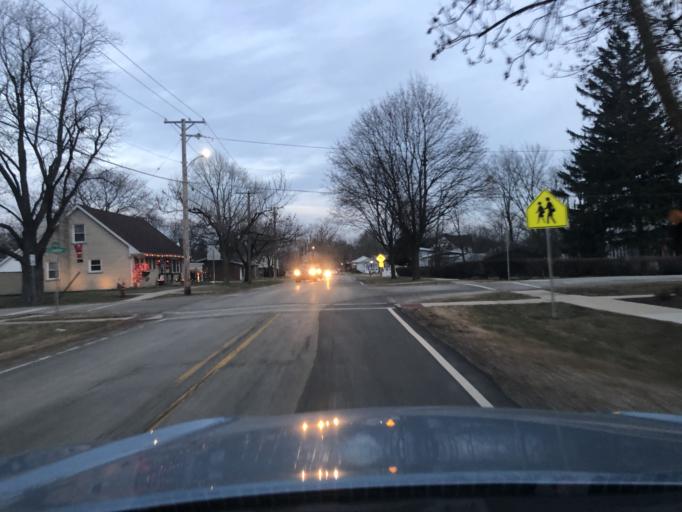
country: US
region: Illinois
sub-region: DuPage County
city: Itasca
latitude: 41.9743
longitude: -88.0110
